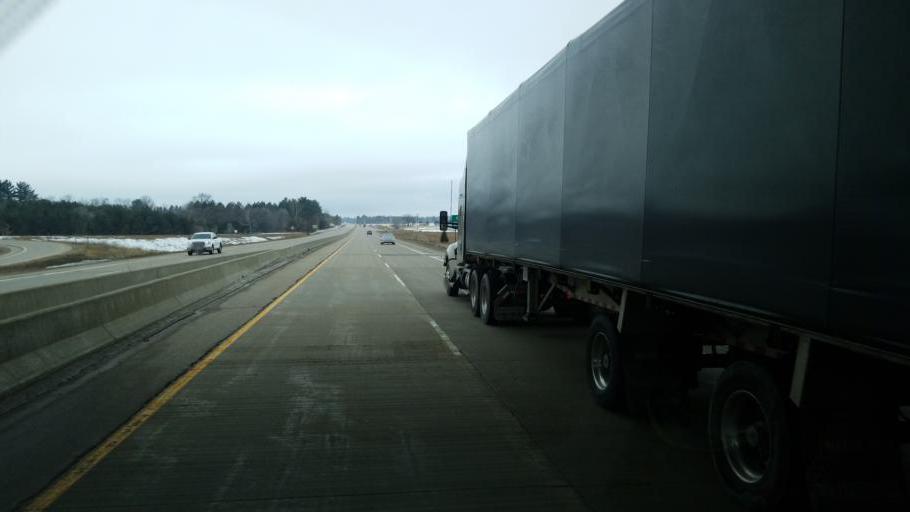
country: US
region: Wisconsin
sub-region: Portage County
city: Whiting
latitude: 44.5212
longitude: -89.4466
